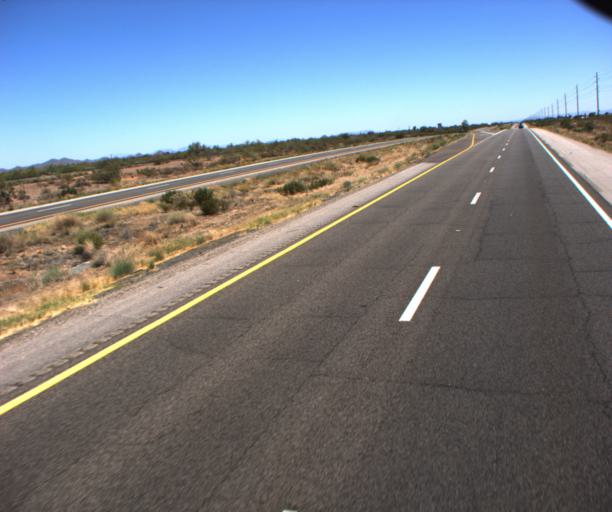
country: US
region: Arizona
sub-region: Maricopa County
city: Wickenburg
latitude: 33.7984
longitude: -112.5552
